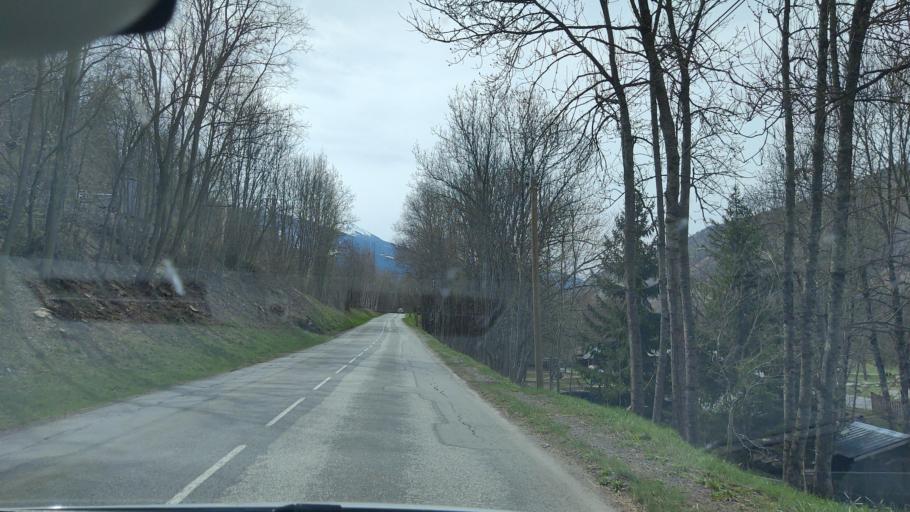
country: FR
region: Rhone-Alpes
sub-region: Departement de la Savoie
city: Bourg-Saint-Maurice
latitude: 45.6012
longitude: 6.7661
